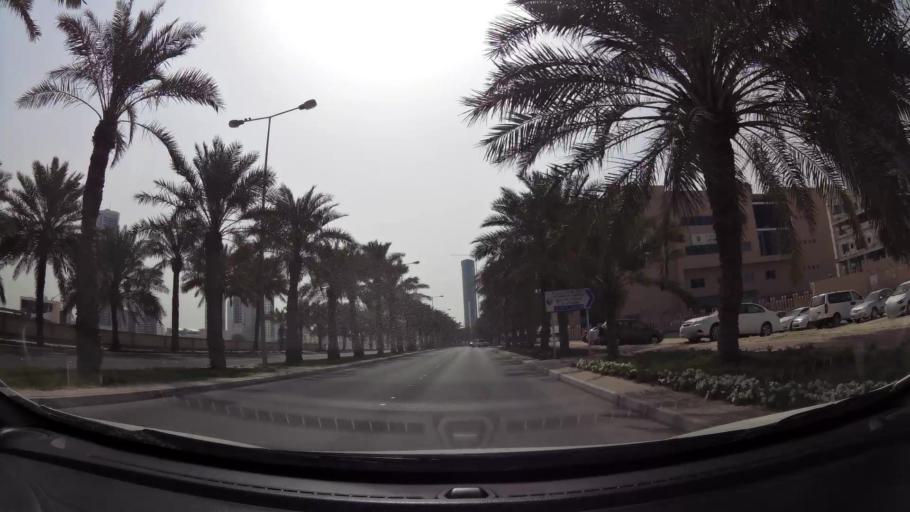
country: BH
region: Manama
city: Jidd Hafs
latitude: 26.2375
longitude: 50.5427
